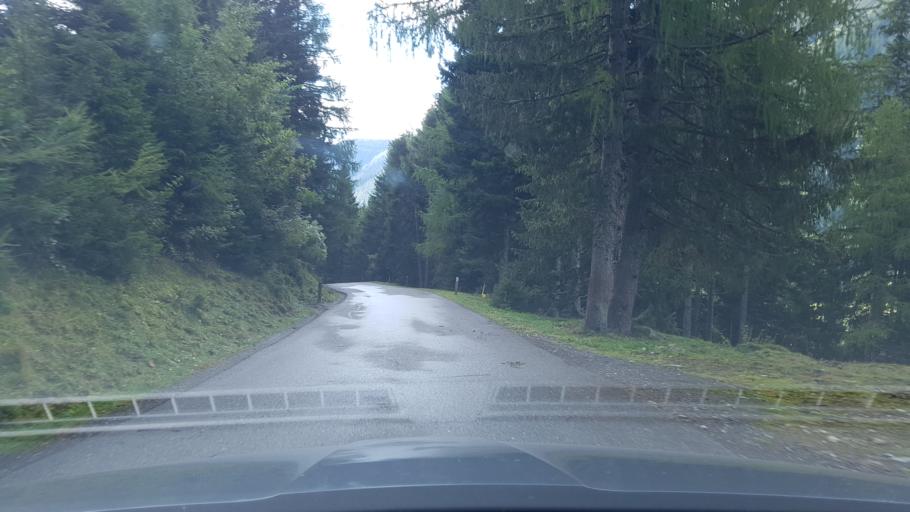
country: AT
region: Styria
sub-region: Politischer Bezirk Liezen
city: Sankt Nikolai im Solktal
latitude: 47.2551
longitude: 14.0817
